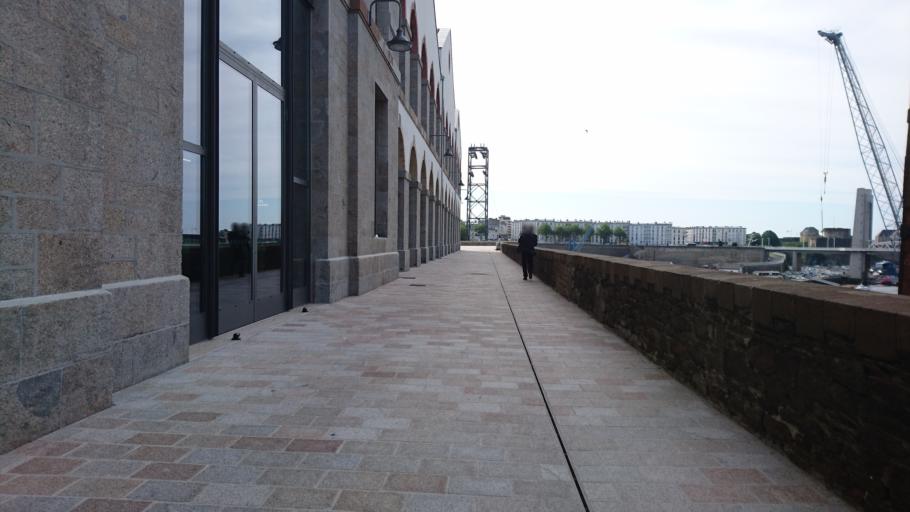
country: FR
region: Brittany
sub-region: Departement du Finistere
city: Brest
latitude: 48.3886
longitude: -4.4984
